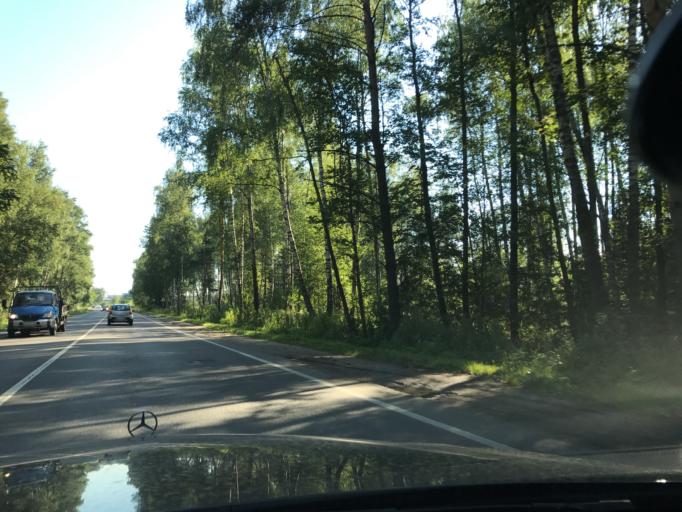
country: RU
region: Moskovskaya
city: Chernogolovka
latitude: 55.9974
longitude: 38.3589
